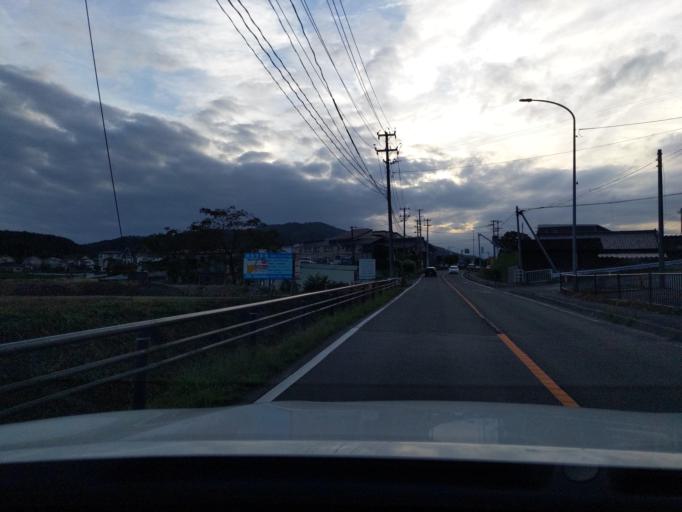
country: JP
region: Miyagi
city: Sendai
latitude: 38.2645
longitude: 140.8217
